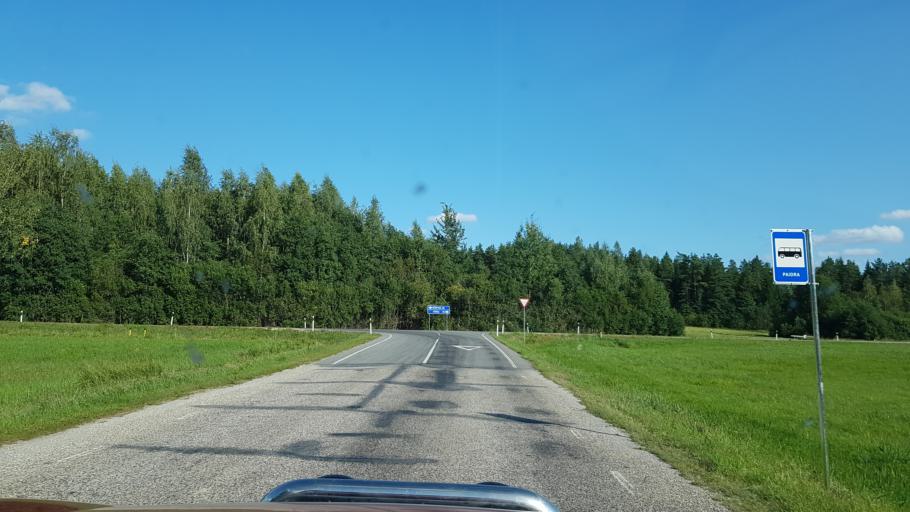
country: EE
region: Vorumaa
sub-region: Voru linn
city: Voru
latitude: 57.9150
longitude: 27.1771
